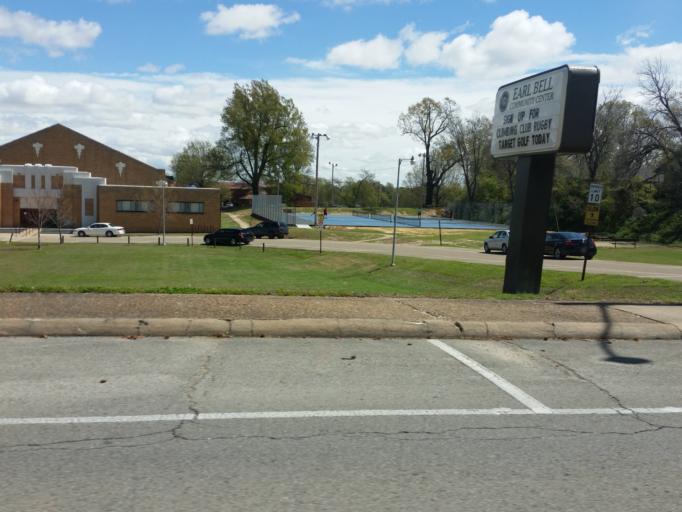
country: US
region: Arkansas
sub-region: Craighead County
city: Jonesboro
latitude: 35.8314
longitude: -90.7042
